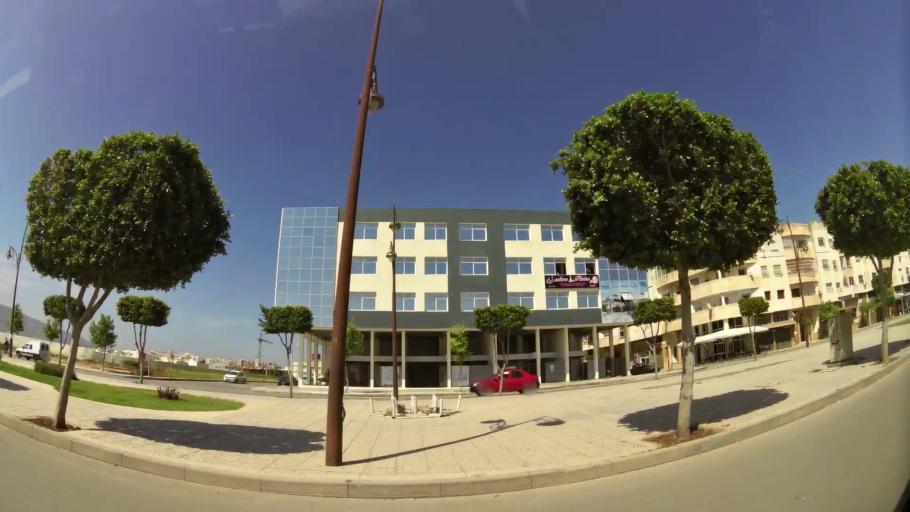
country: MA
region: Fes-Boulemane
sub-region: Fes
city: Fes
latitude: 34.0184
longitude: -5.0211
